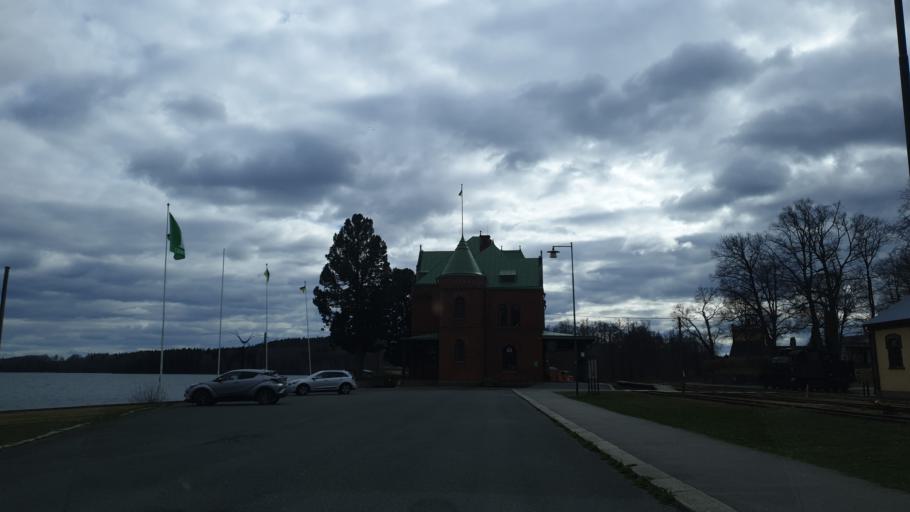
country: SE
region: OErebro
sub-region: Nora Kommun
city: Nora
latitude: 59.5170
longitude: 15.0424
